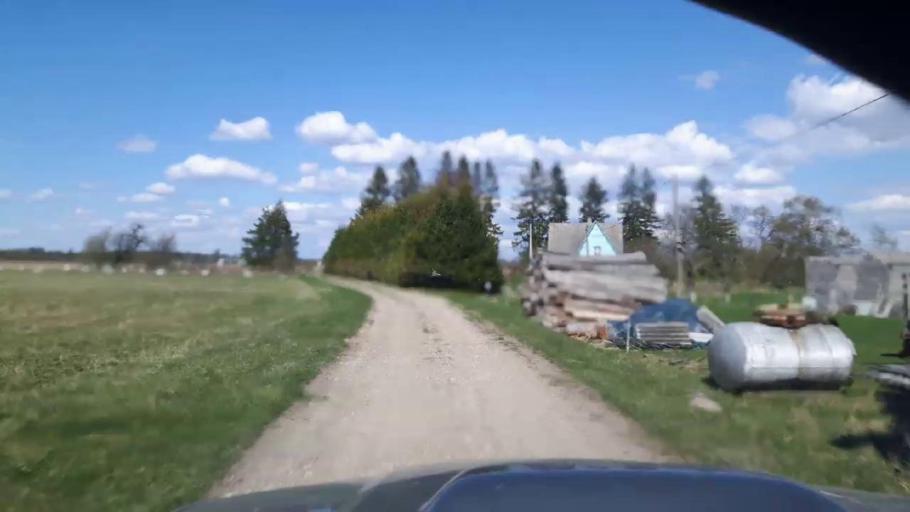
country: EE
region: Paernumaa
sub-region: Tootsi vald
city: Tootsi
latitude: 58.4656
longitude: 24.7993
